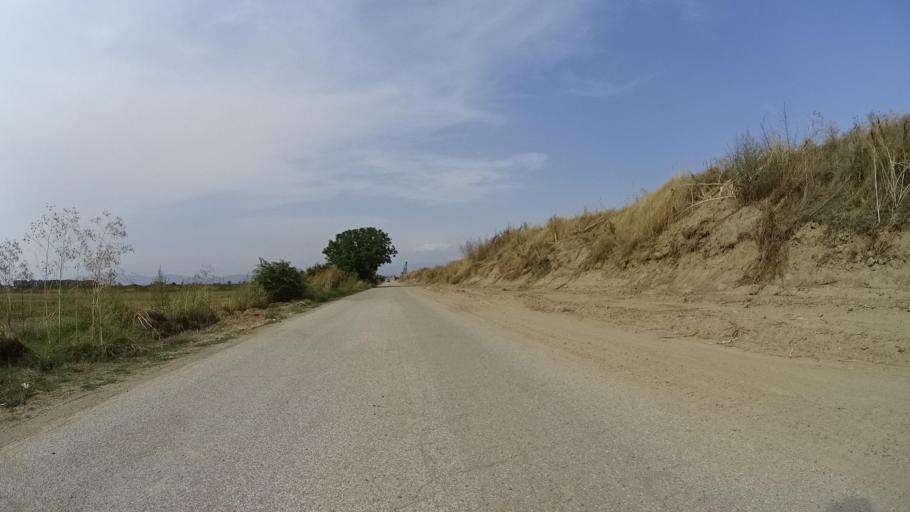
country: BG
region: Plovdiv
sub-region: Obshtina Kaloyanovo
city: Kaloyanovo
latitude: 42.3093
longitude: 24.7996
